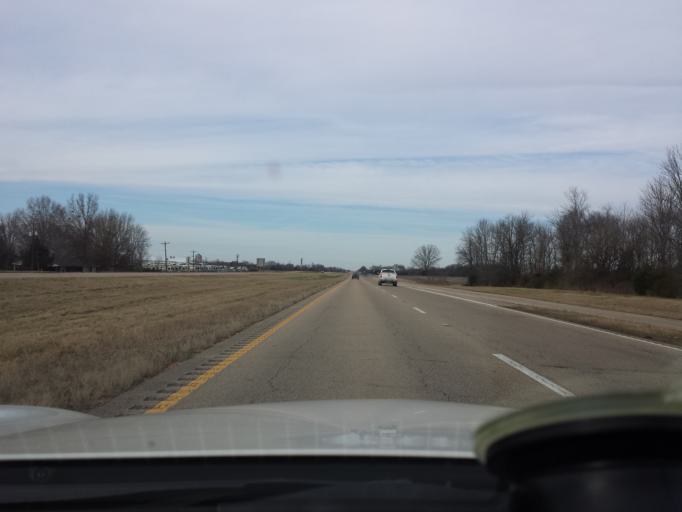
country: US
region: Mississippi
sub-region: Chickasaw County
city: Okolona
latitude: 33.8441
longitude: -88.7123
